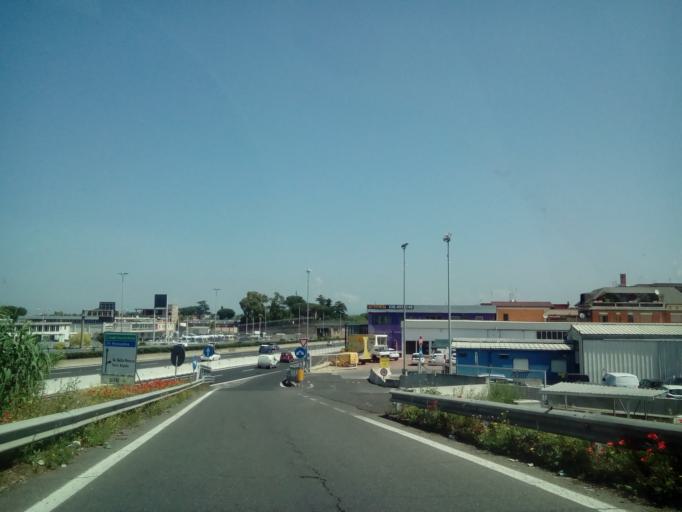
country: IT
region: Latium
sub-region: Citta metropolitana di Roma Capitale
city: Setteville
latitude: 41.8829
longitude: 12.6120
